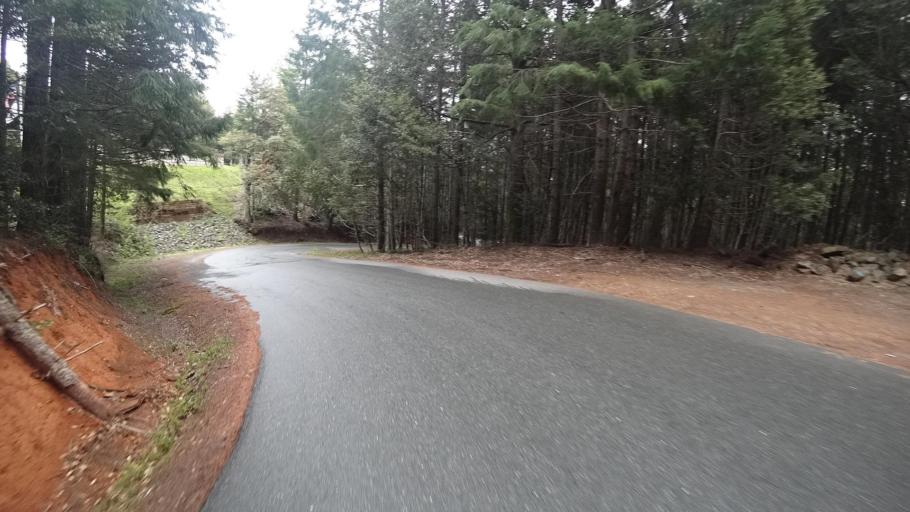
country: US
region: California
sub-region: Humboldt County
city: Willow Creek
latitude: 41.1982
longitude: -123.7842
